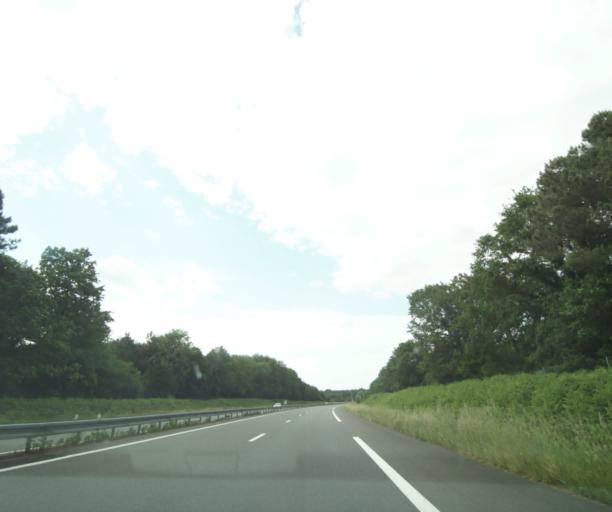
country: FR
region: Pays de la Loire
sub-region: Departement de Maine-et-Loire
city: Brion
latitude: 47.4373
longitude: -0.1714
